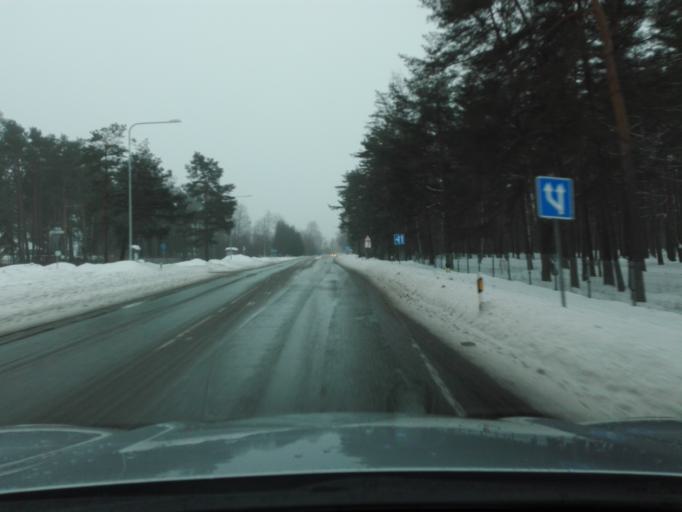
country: EE
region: Harju
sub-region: Kiili vald
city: Kiili
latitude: 59.3342
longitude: 24.7738
